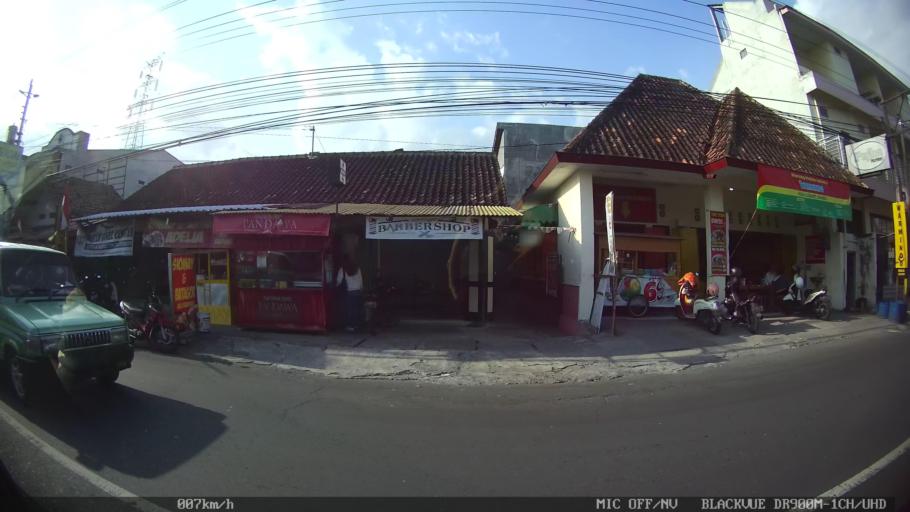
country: ID
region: Daerah Istimewa Yogyakarta
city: Yogyakarta
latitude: -7.7793
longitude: 110.3430
